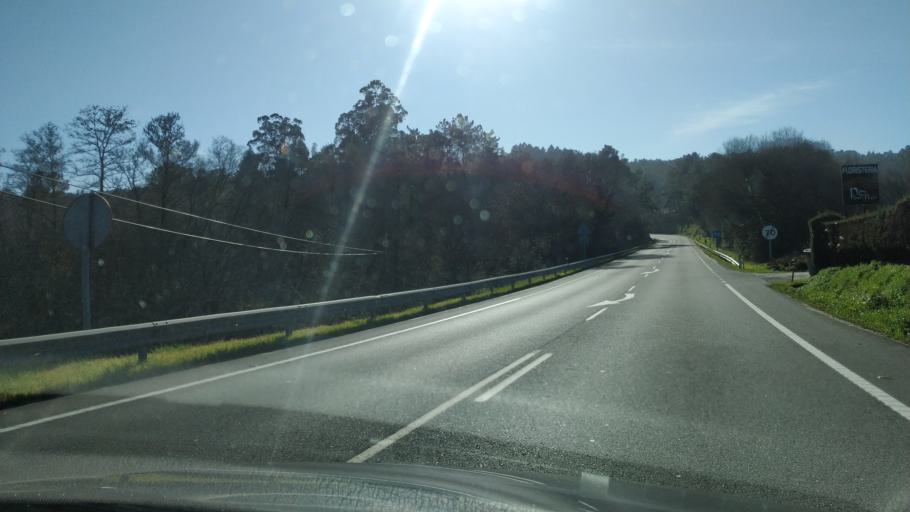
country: ES
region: Galicia
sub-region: Provincia de Pontevedra
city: Silleda
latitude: 42.7328
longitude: -8.3197
